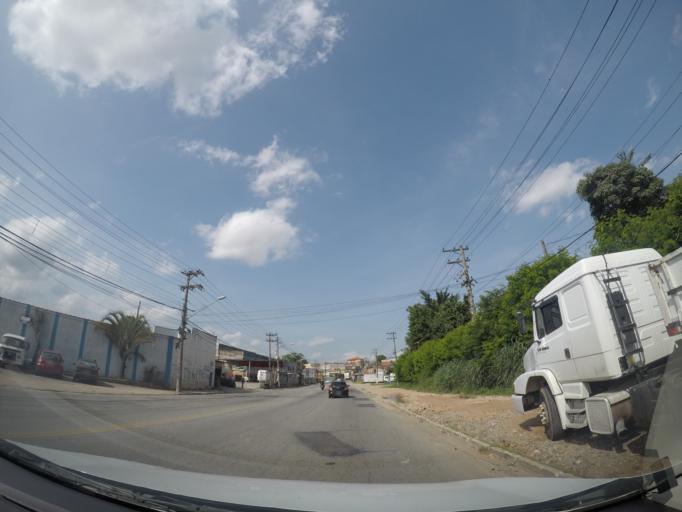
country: BR
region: Sao Paulo
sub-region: Guarulhos
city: Guarulhos
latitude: -23.4351
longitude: -46.4439
